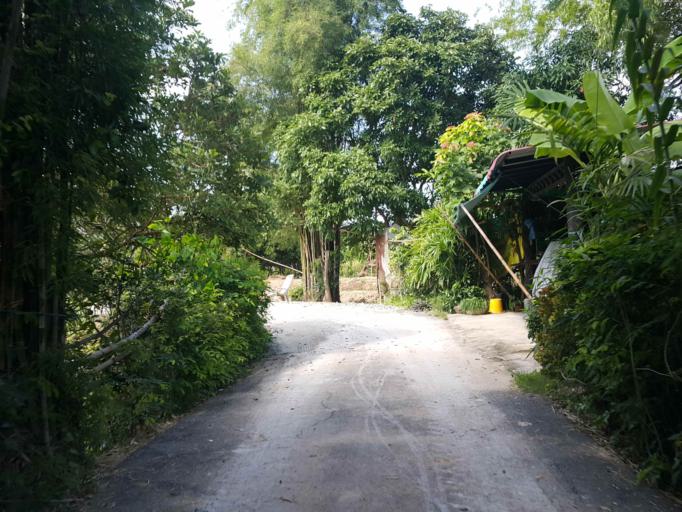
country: TH
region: Chiang Mai
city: San Kamphaeng
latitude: 18.8009
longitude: 99.0898
